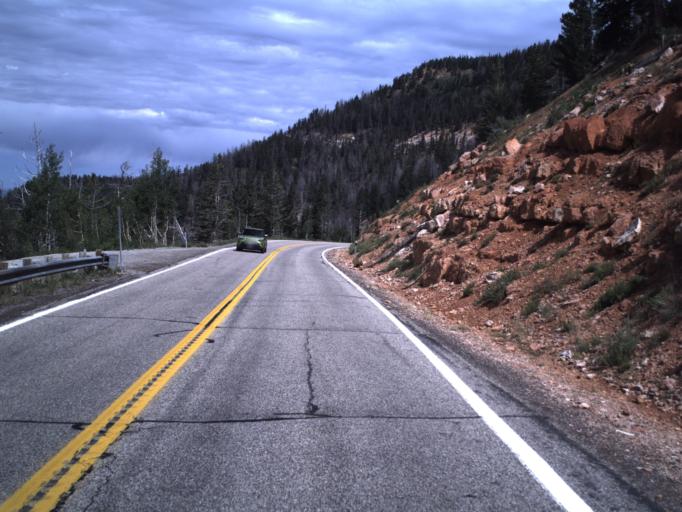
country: US
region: Utah
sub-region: Iron County
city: Cedar City
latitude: 37.5723
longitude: -112.8595
